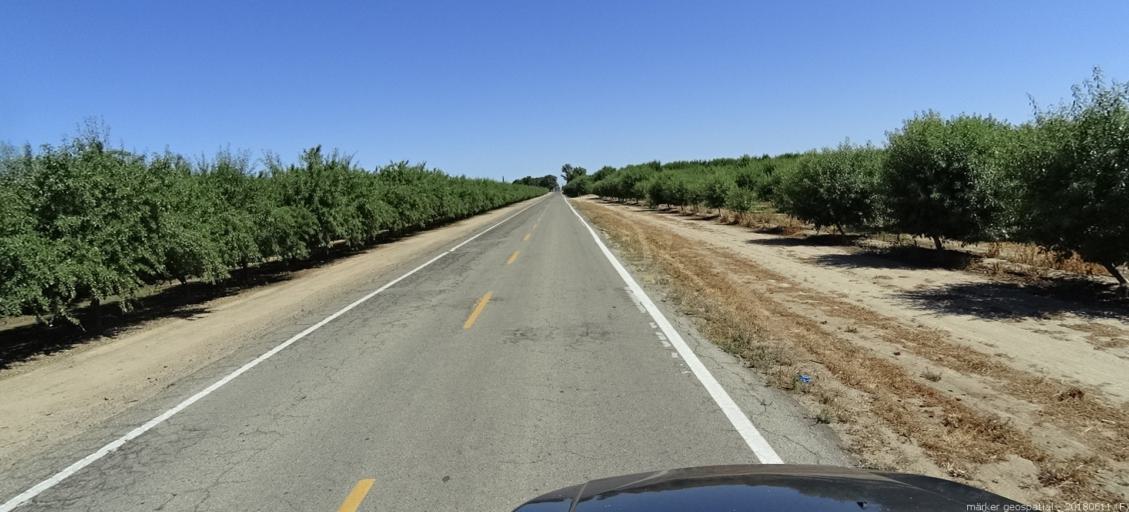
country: US
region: California
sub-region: Madera County
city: Fairmead
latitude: 37.0062
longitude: -120.2024
